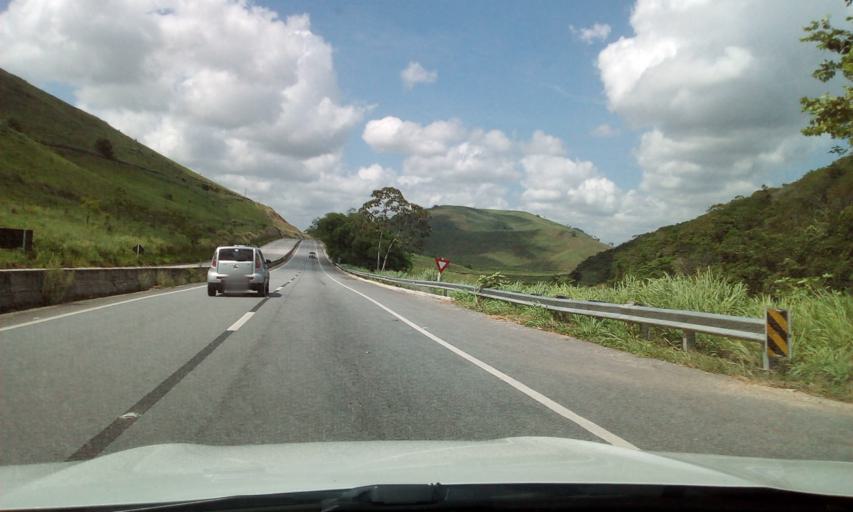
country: BR
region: Alagoas
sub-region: Flexeiras
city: Flexeiras
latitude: -9.2487
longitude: -35.7666
